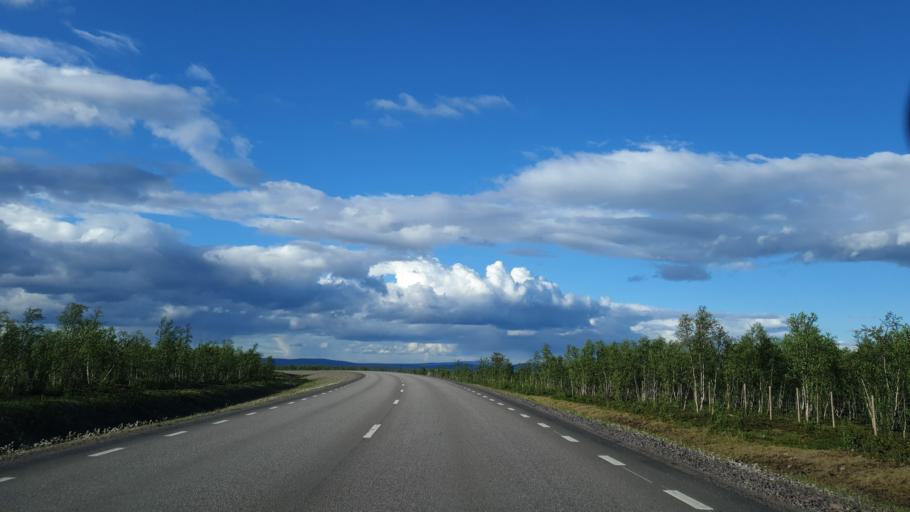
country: SE
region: Norrbotten
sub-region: Kiruna Kommun
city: Kiruna
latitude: 67.8277
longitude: 20.2970
